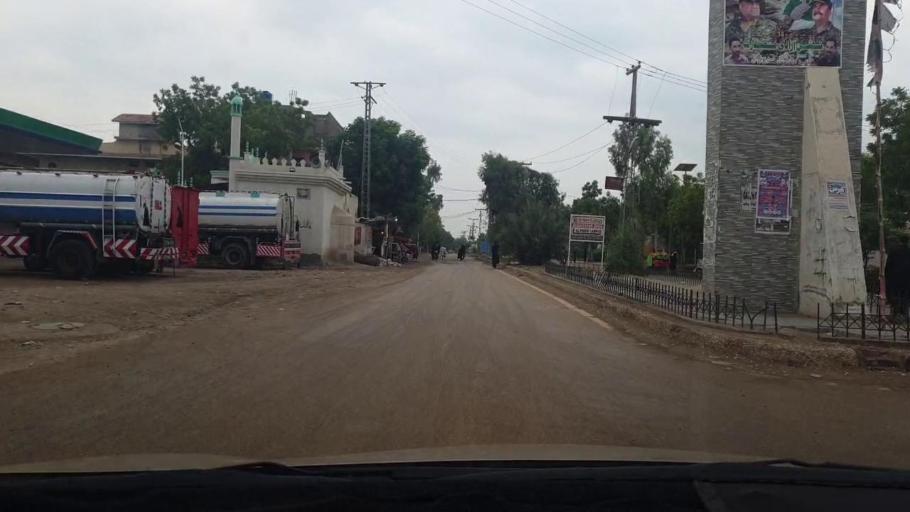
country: PK
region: Sindh
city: Larkana
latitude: 27.5642
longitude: 68.1976
